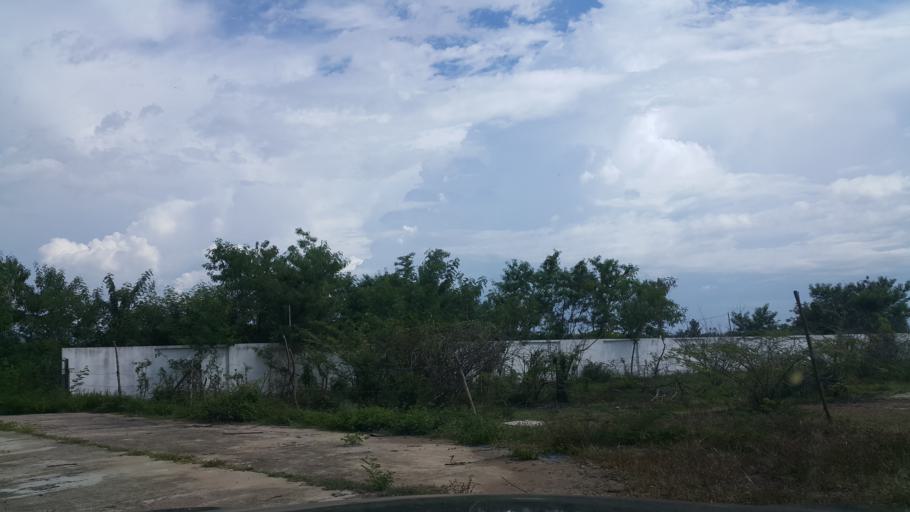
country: TH
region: Chiang Mai
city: San Kamphaeng
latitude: 18.7172
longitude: 99.1562
